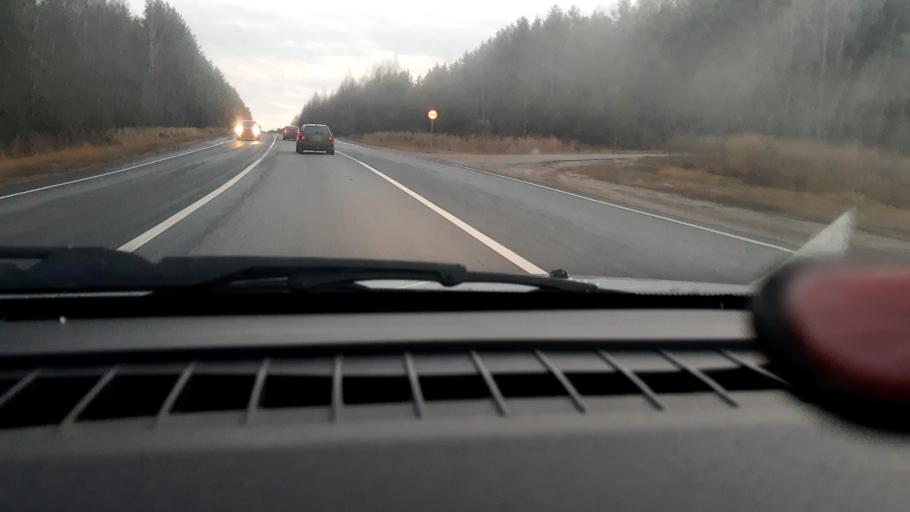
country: RU
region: Nizjnij Novgorod
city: Krasnyye Baki
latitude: 57.0284
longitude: 45.1154
